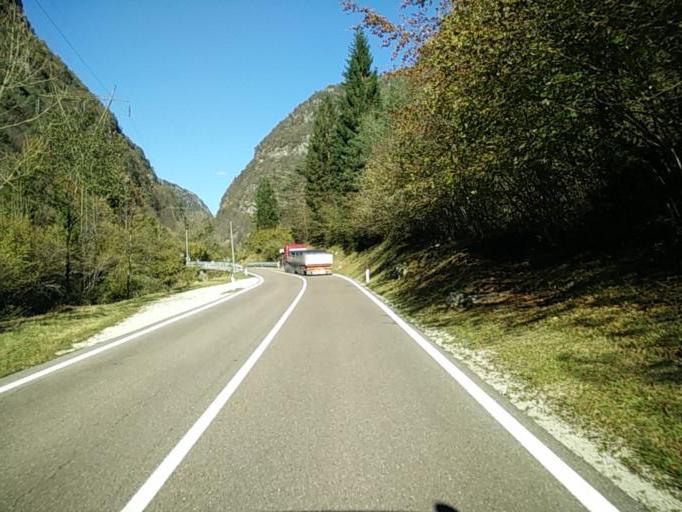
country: IT
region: Trentino-Alto Adige
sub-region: Provincia di Trento
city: Condino
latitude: 45.8502
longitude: 10.6333
